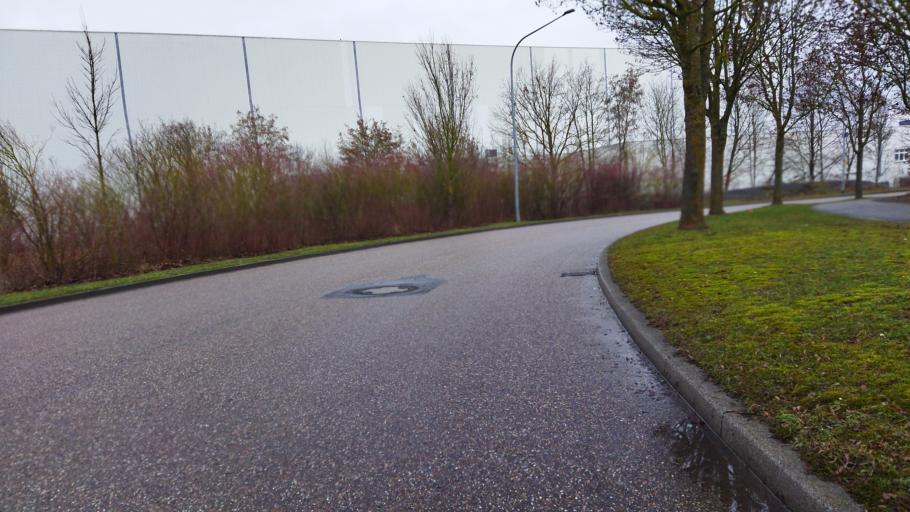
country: DE
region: Baden-Wuerttemberg
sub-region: Regierungsbezirk Stuttgart
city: Bad Wimpfen
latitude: 49.1836
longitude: 9.1611
